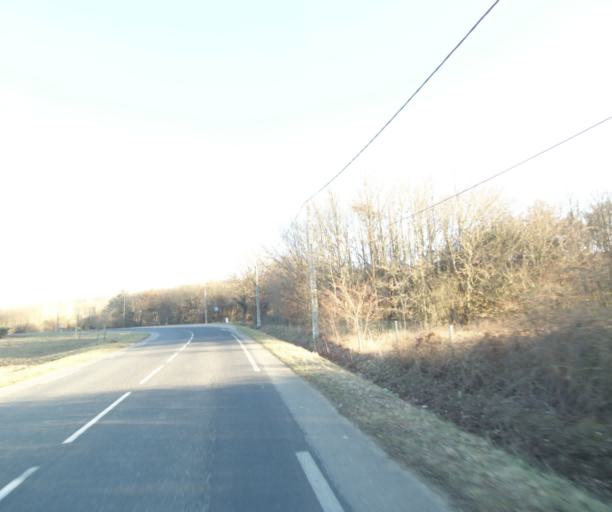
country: FR
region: Lorraine
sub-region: Departement de Meurthe-et-Moselle
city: Seichamps
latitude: 48.7032
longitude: 6.2716
